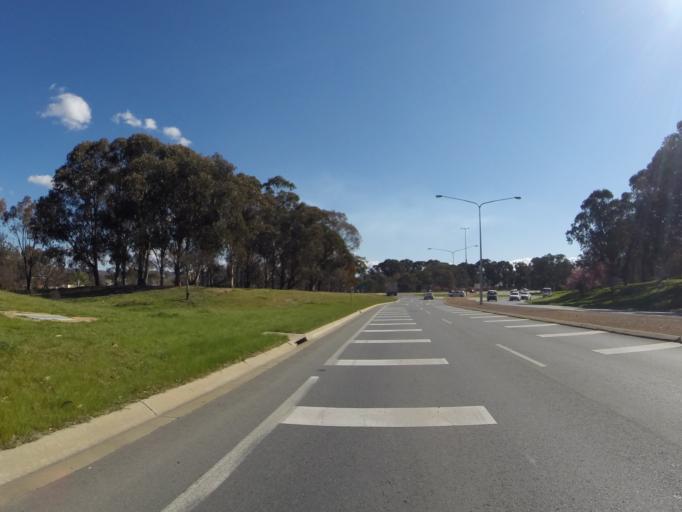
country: AU
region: Australian Capital Territory
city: Forrest
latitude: -35.3024
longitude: 149.1534
